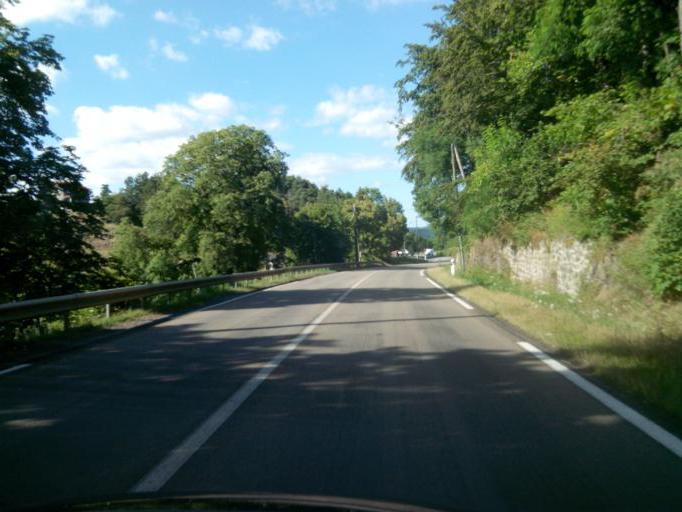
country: FR
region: Auvergne
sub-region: Departement de la Haute-Loire
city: Polignac
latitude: 45.0637
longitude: 3.8496
